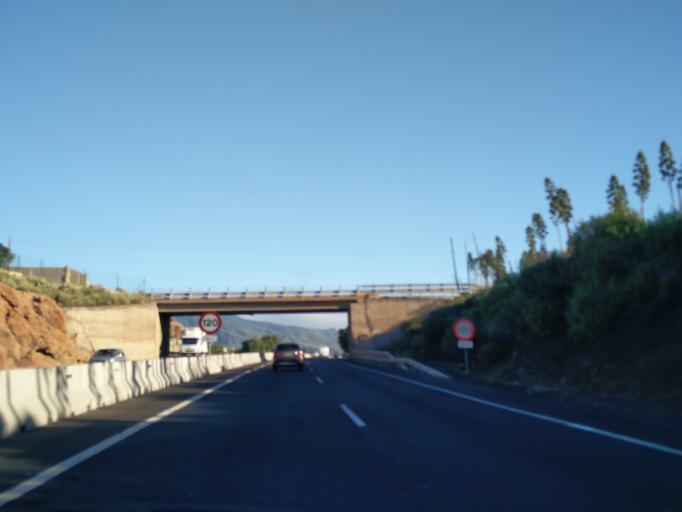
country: ES
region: Canary Islands
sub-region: Provincia de Santa Cruz de Tenerife
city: Candelaria
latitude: 28.3087
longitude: -16.3831
